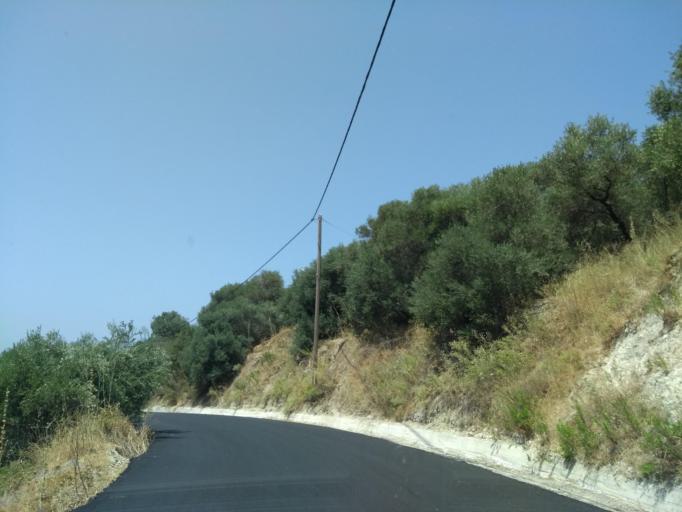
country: GR
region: Crete
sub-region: Nomos Chanias
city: Georgioupolis
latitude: 35.3241
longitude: 24.2999
